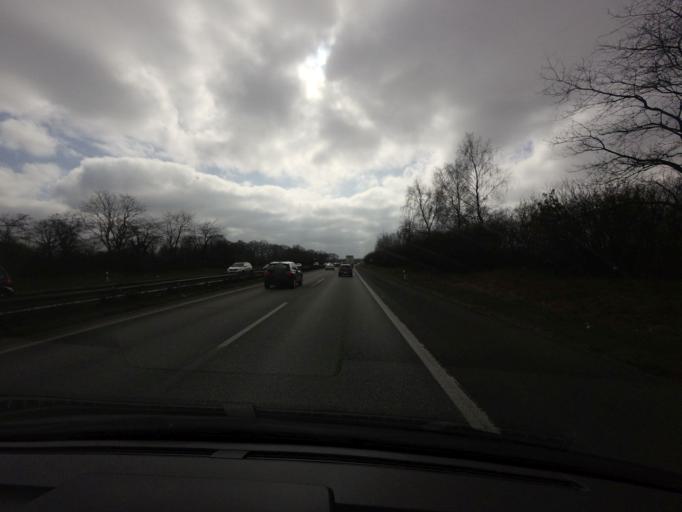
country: DE
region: Schleswig-Holstein
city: Schmalfeld
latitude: 53.8754
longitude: 9.9470
